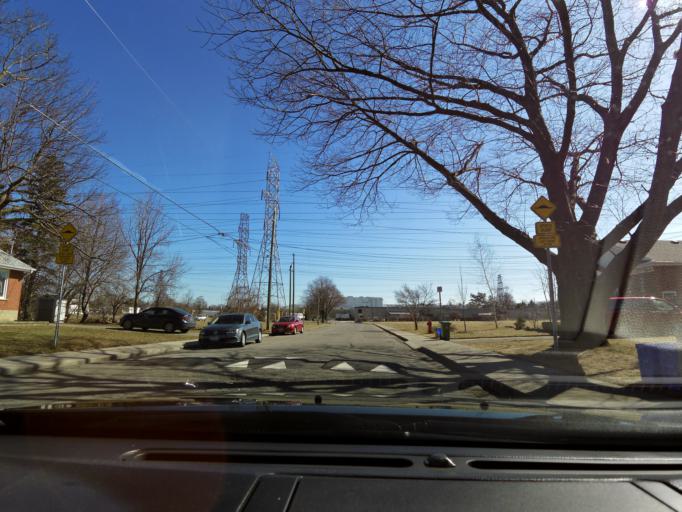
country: CA
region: Ontario
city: Ancaster
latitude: 43.2552
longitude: -79.9342
